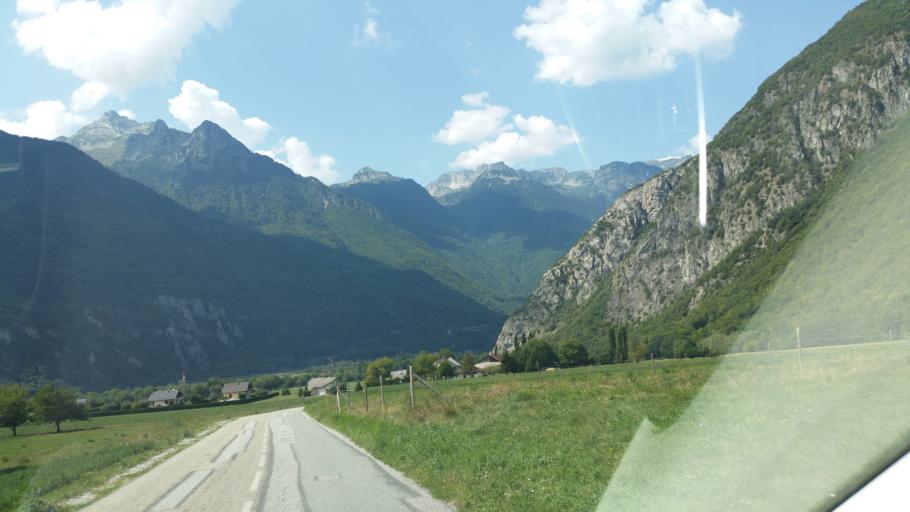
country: FR
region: Rhone-Alpes
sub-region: Departement de la Savoie
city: La Chambre
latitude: 45.3651
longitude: 6.3026
